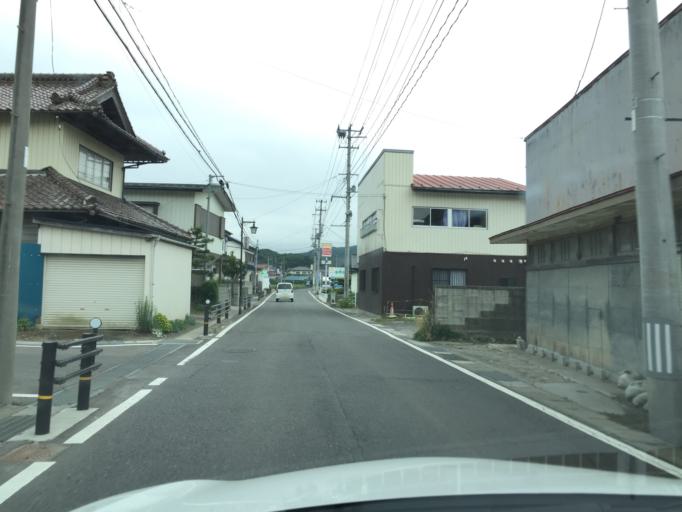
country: JP
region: Fukushima
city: Funehikimachi-funehiki
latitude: 37.3744
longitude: 140.6387
